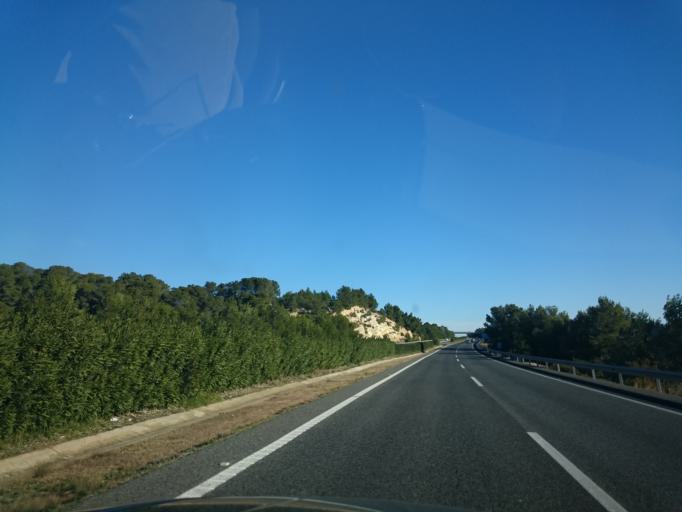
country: ES
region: Catalonia
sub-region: Provincia de Tarragona
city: El Perello
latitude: 40.8464
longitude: 0.7506
